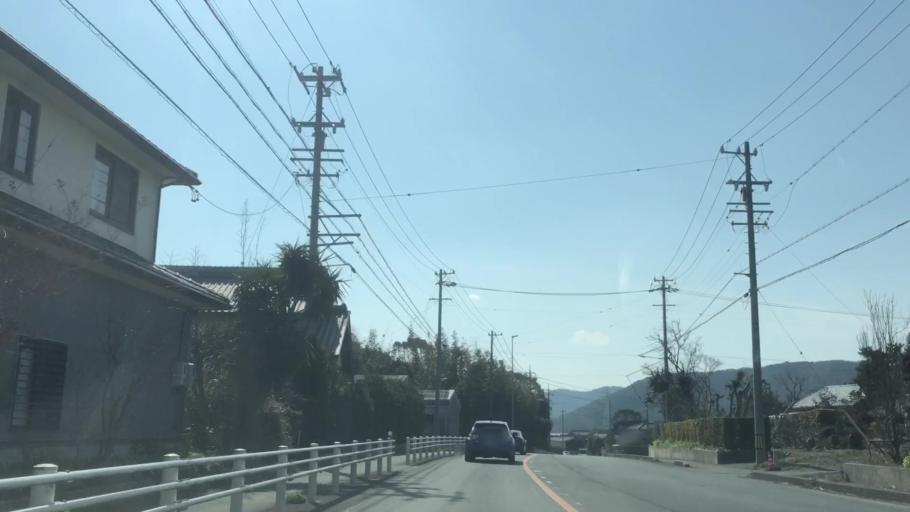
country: JP
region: Aichi
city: Tahara
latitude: 34.6457
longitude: 137.2409
